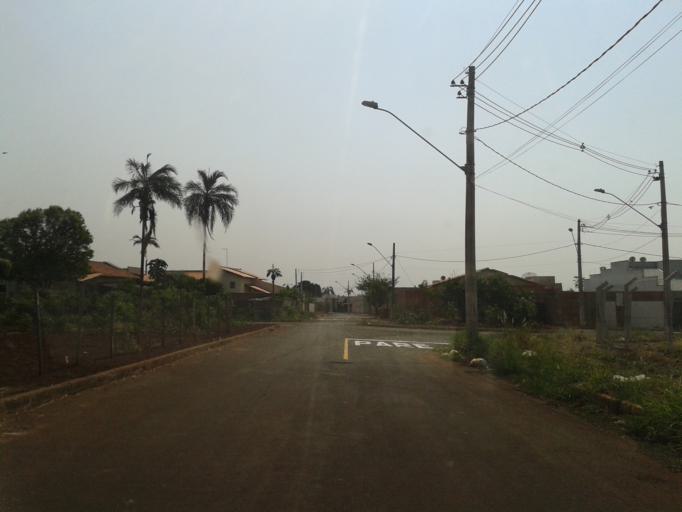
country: BR
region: Minas Gerais
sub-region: Ituiutaba
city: Ituiutaba
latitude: -18.9622
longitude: -49.4488
